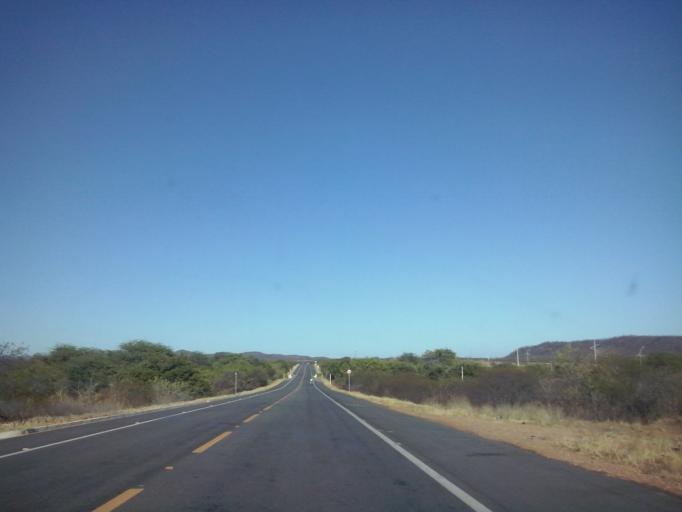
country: BR
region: Paraiba
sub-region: Pombal
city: Pombal
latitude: -6.9118
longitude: -37.6082
